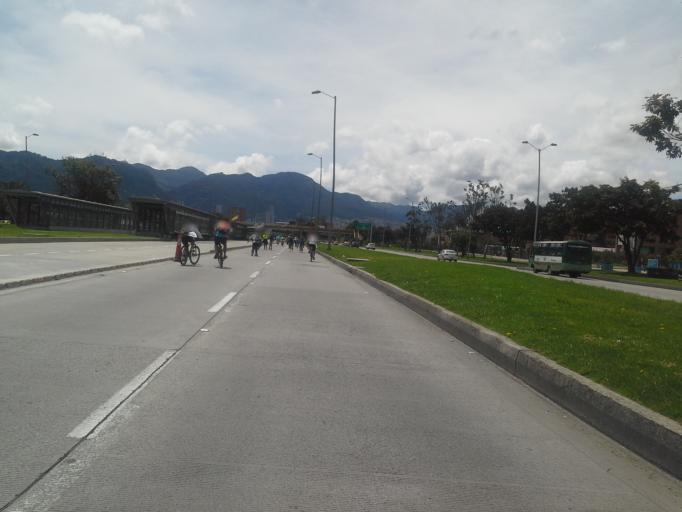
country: CO
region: Bogota D.C.
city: Bogota
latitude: 4.6437
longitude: -74.0973
